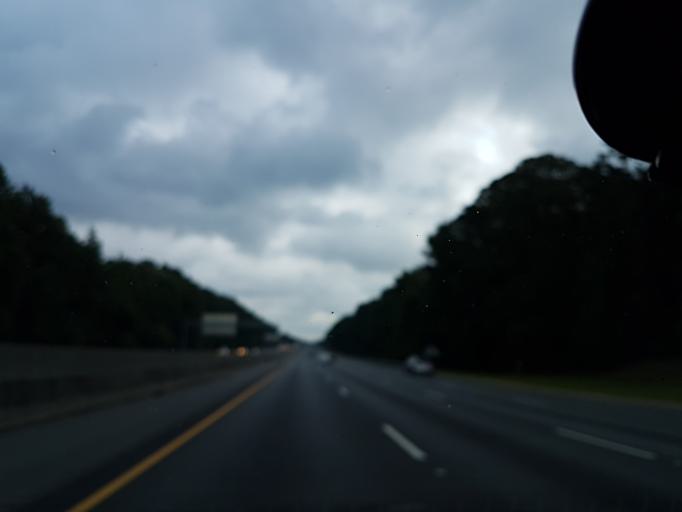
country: US
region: Georgia
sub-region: DeKalb County
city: Clarkston
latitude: 33.8202
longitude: -84.2431
